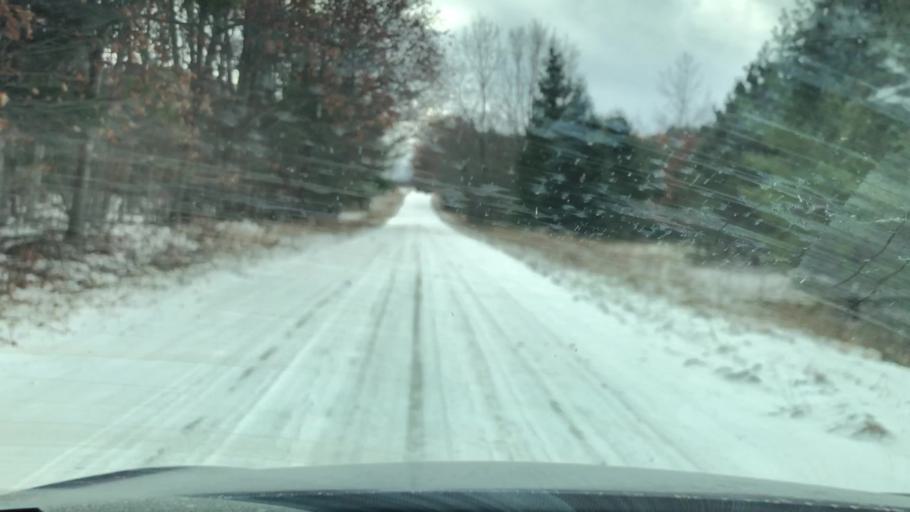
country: US
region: Michigan
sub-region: Antrim County
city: Elk Rapids
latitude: 44.9573
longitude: -85.5155
